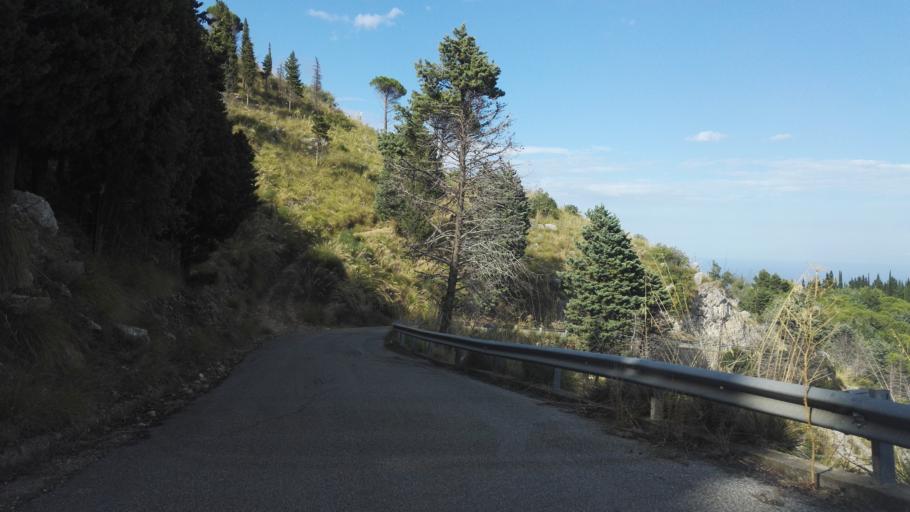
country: IT
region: Calabria
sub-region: Provincia di Reggio Calabria
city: Pazzano
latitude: 38.4687
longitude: 16.4463
